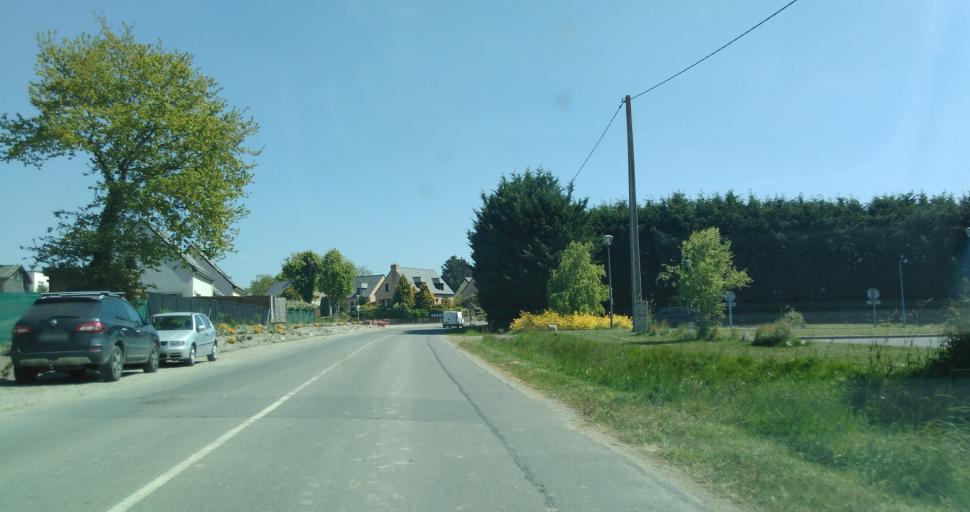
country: FR
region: Brittany
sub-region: Departement d'Ille-et-Vilaine
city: Saint-Gilles
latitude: 48.1284
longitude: -1.8242
